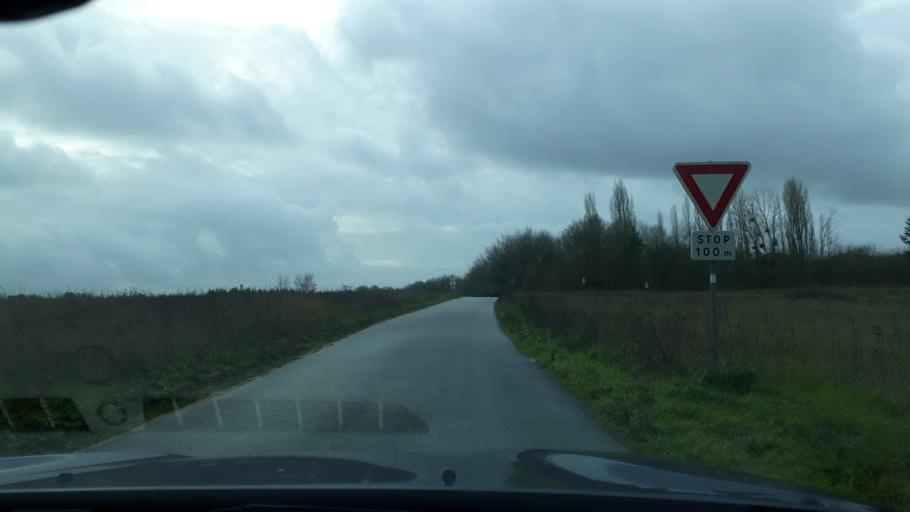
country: FR
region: Centre
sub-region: Departement du Loiret
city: Clery-Saint-Andre
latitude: 47.8173
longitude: 1.7767
